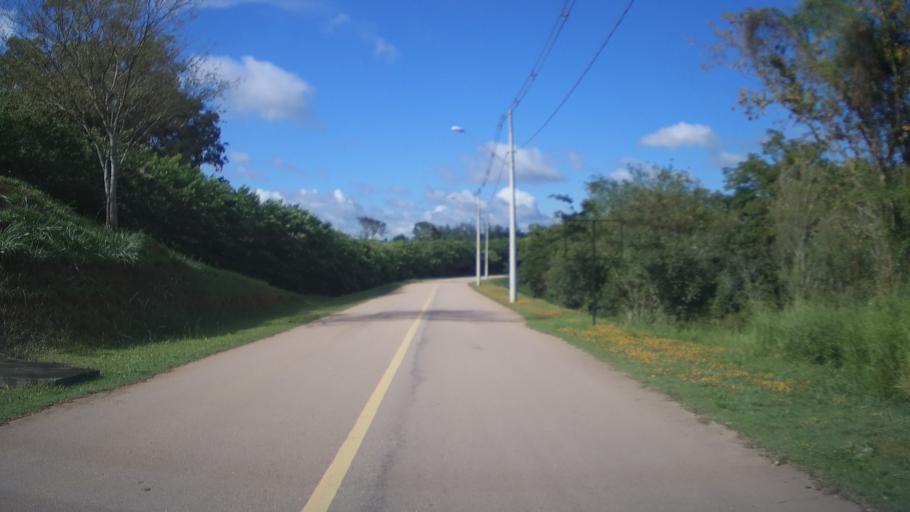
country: BR
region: Sao Paulo
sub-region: Itupeva
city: Itupeva
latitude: -23.2018
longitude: -47.0250
